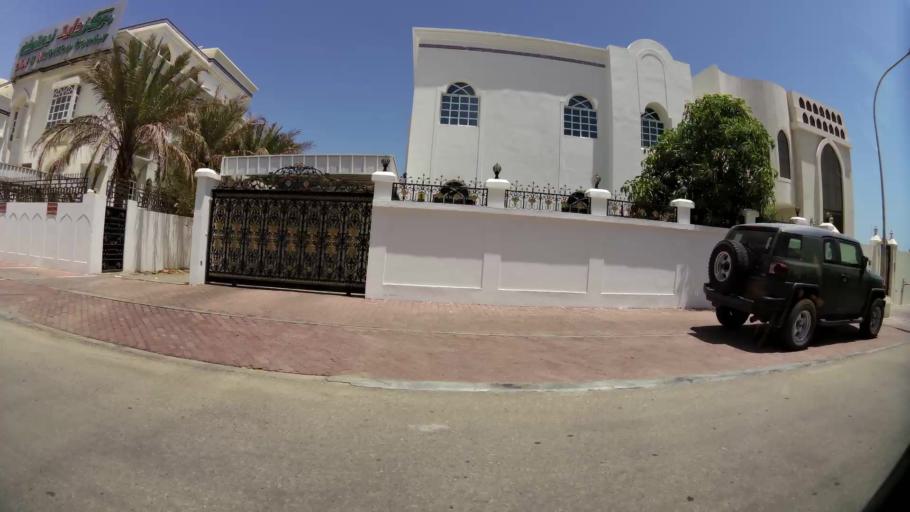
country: OM
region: Muhafazat Masqat
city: Bawshar
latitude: 23.6102
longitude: 58.4584
